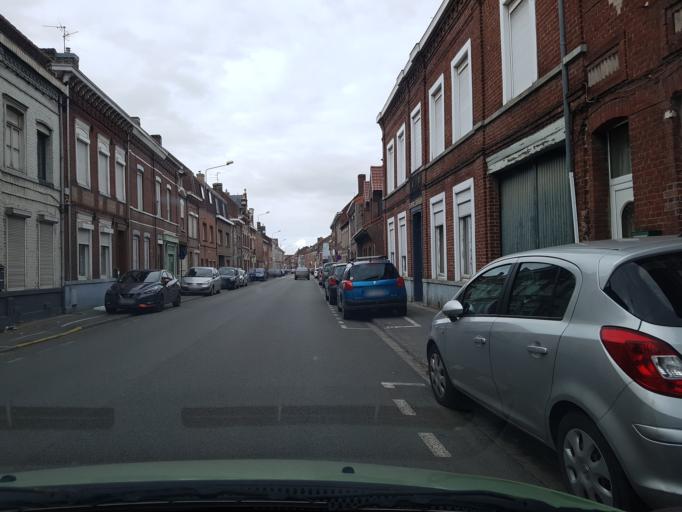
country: FR
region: Nord-Pas-de-Calais
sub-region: Departement du Nord
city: Annoeullin
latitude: 50.5252
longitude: 2.9356
